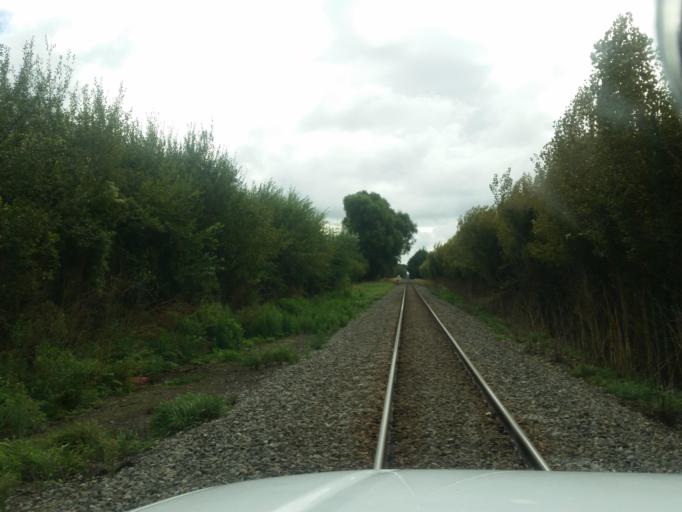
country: NZ
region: Canterbury
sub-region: Christchurch City
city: Christchurch
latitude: -43.4611
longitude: 172.6260
